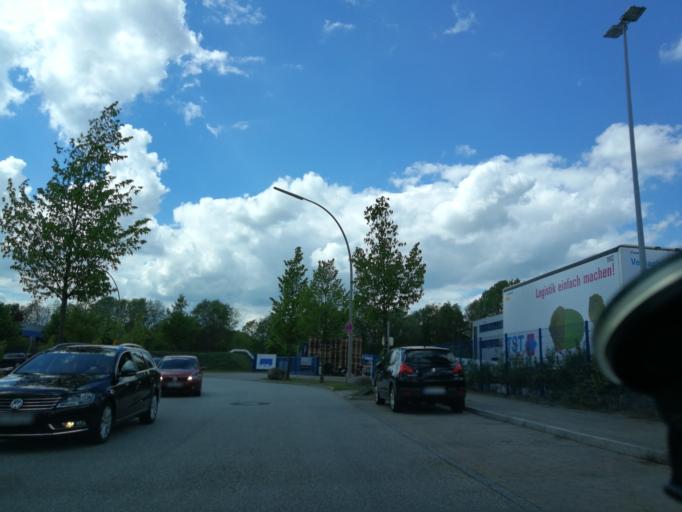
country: DE
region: Hamburg
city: Altona
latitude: 53.4808
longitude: 9.9026
